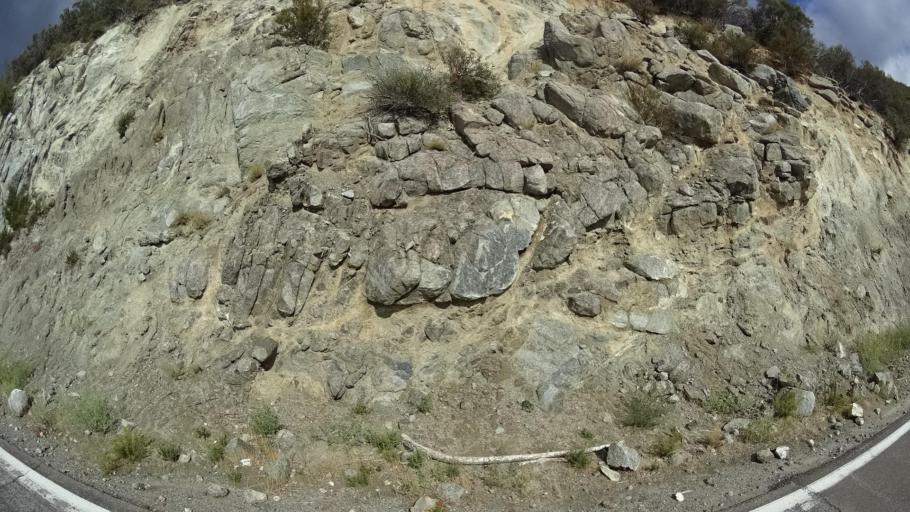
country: US
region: California
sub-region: San Diego County
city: Pine Valley
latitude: 32.8179
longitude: -116.5099
